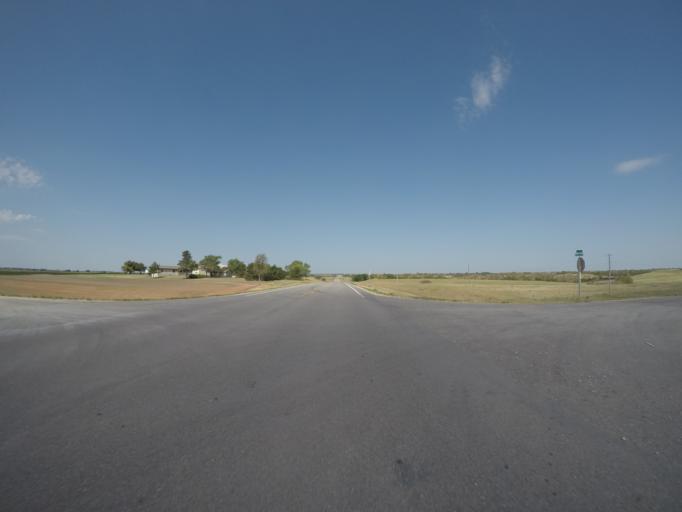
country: US
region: Kansas
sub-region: Clay County
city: Clay Center
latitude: 39.3785
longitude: -97.3505
